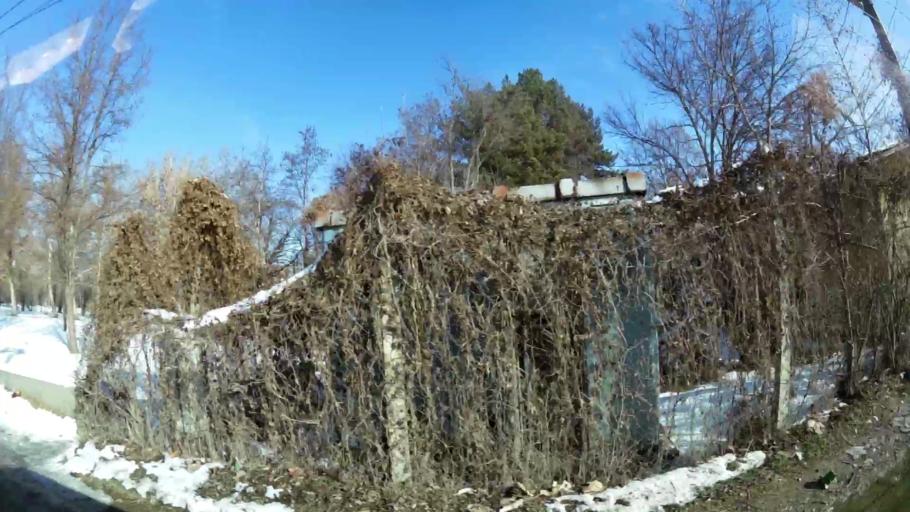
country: MK
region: Saraj
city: Saraj
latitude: 41.9994
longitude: 21.3405
